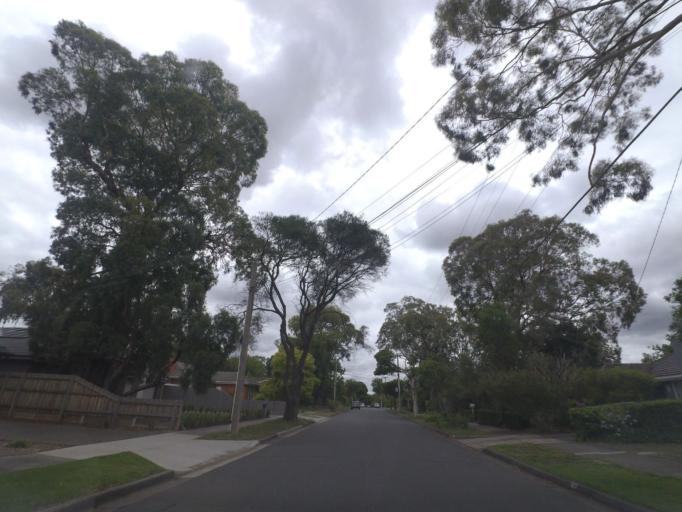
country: AU
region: Victoria
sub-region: Whitehorse
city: Forest Hill
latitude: -37.8305
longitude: 145.1687
